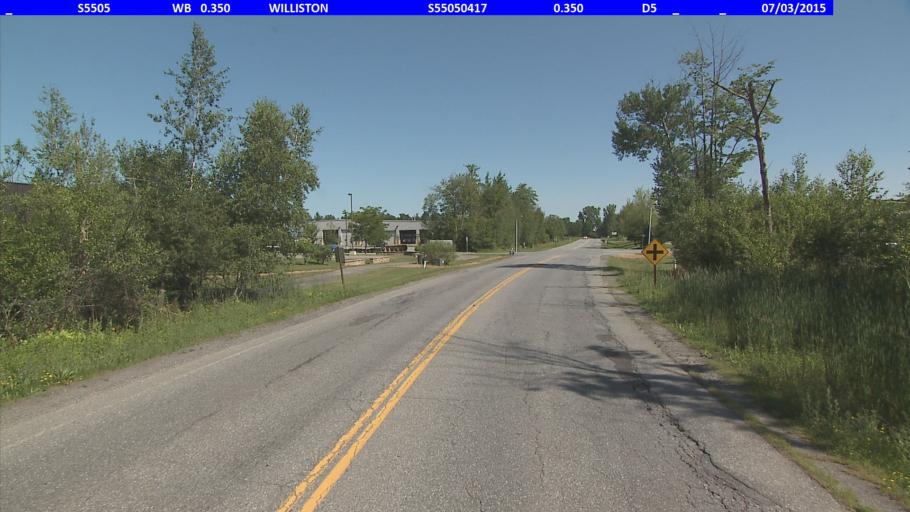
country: US
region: Vermont
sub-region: Chittenden County
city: South Burlington
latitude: 44.4481
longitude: -73.1348
